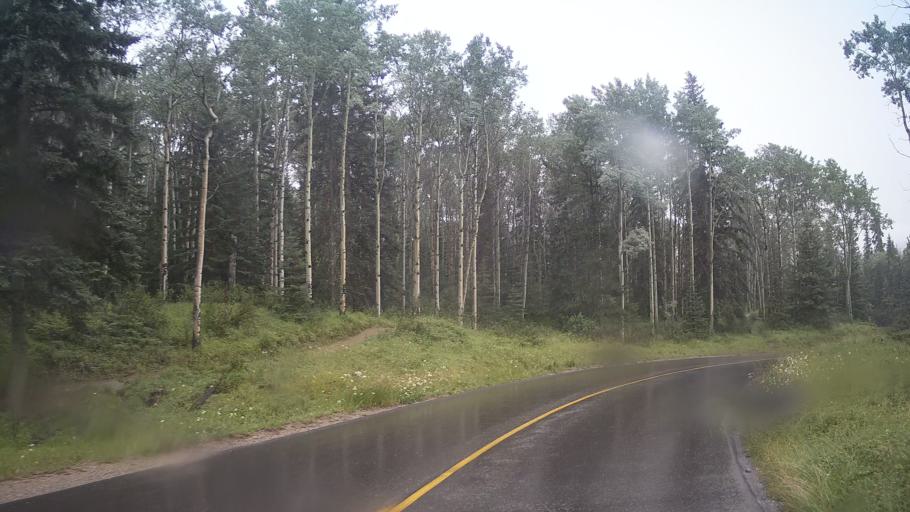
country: CA
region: Alberta
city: Jasper Park Lodge
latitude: 52.9123
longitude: -118.0924
